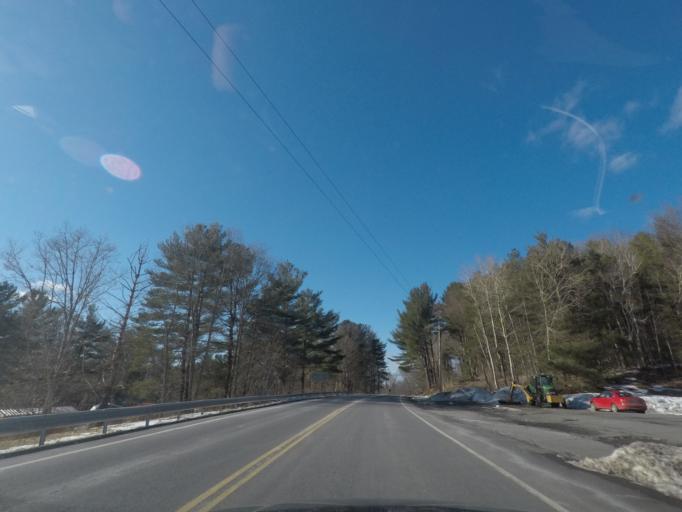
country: US
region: Massachusetts
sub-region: Berkshire County
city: Richmond
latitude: 42.3943
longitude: -73.4126
